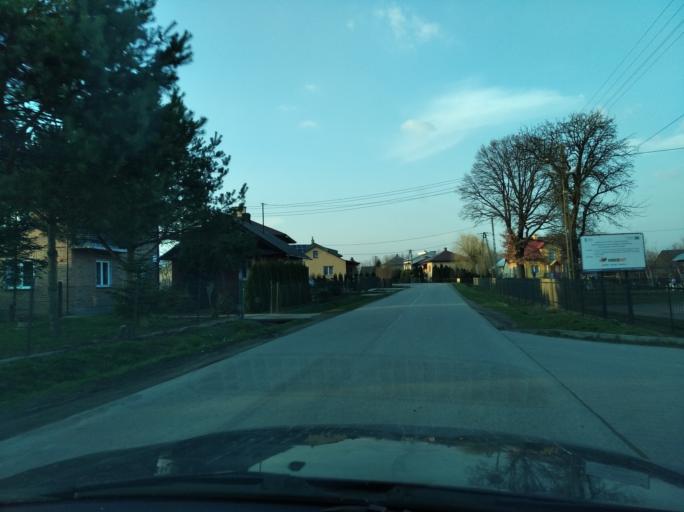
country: PL
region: Subcarpathian Voivodeship
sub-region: Powiat przeworski
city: Zarzecze
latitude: 49.9502
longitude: 22.5568
